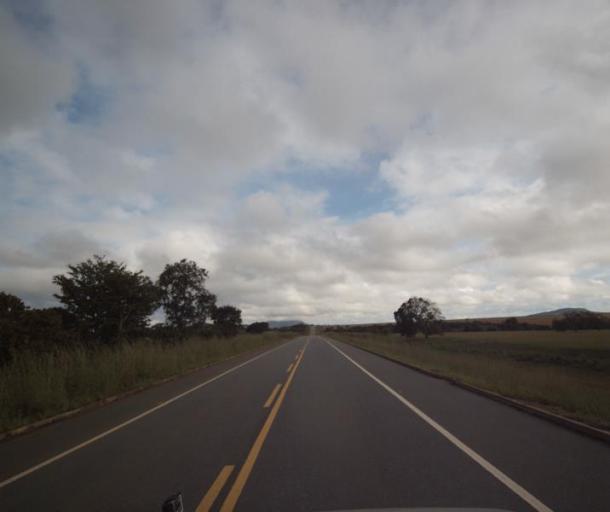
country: BR
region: Goias
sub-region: Padre Bernardo
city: Padre Bernardo
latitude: -15.3054
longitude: -48.6679
